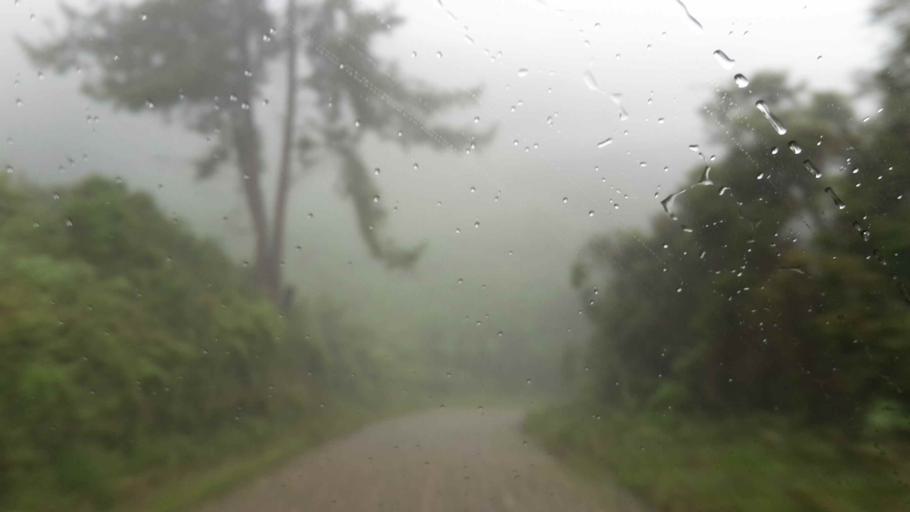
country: BO
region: Cochabamba
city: Colomi
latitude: -17.1523
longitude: -65.9093
